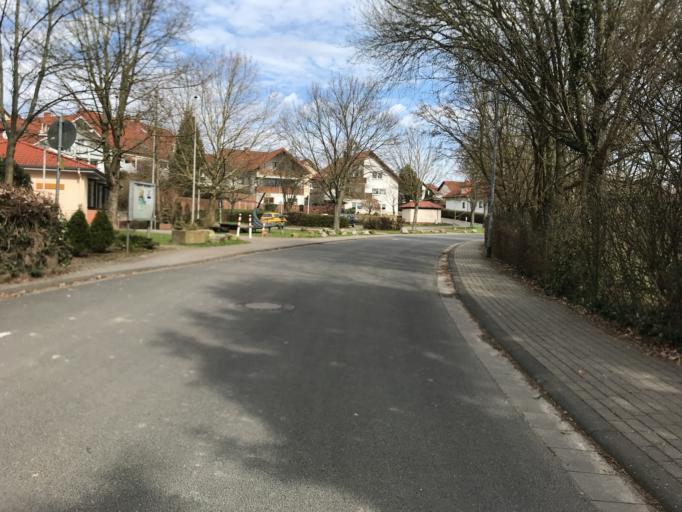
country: DE
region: Rheinland-Pfalz
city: Partenheim
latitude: 49.8835
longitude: 8.0727
